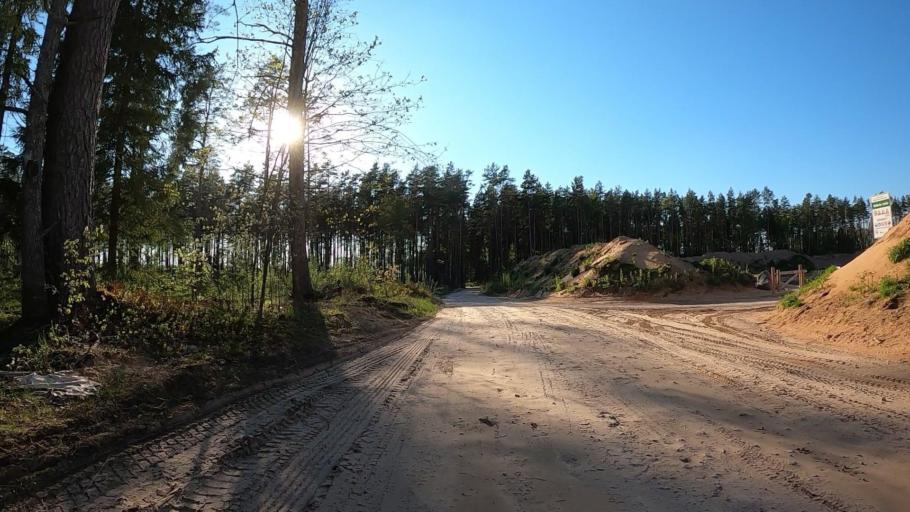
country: LV
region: Kekava
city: Kekava
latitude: 56.7813
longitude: 24.3082
